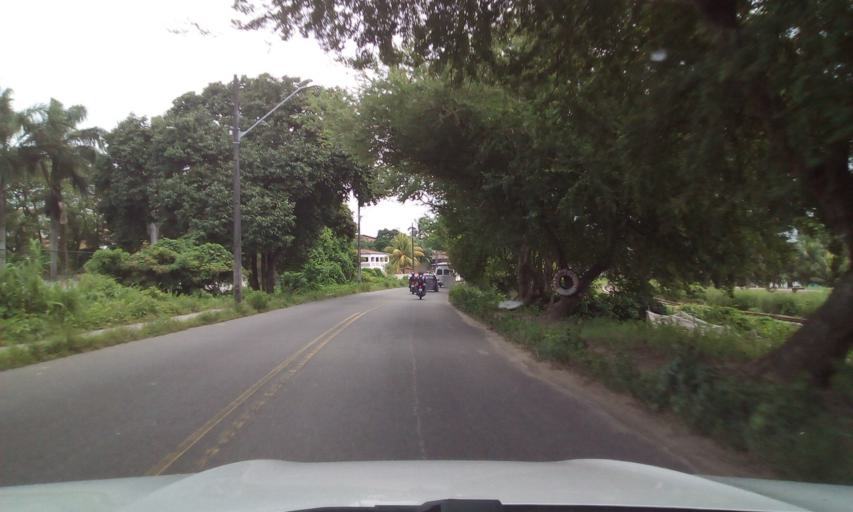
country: BR
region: Paraiba
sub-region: Joao Pessoa
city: Joao Pessoa
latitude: -7.1083
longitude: -34.8811
